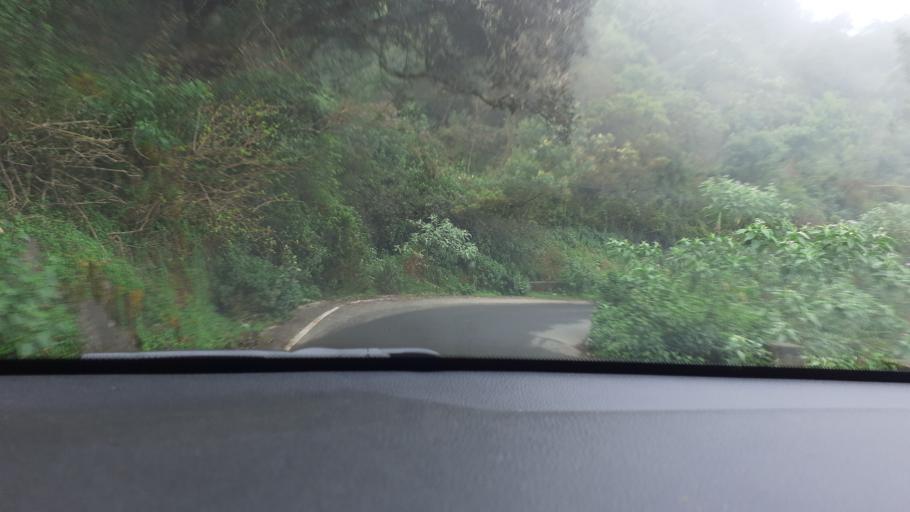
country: IN
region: Tamil Nadu
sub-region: Dindigul
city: Kodaikanal
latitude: 10.2482
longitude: 77.4160
